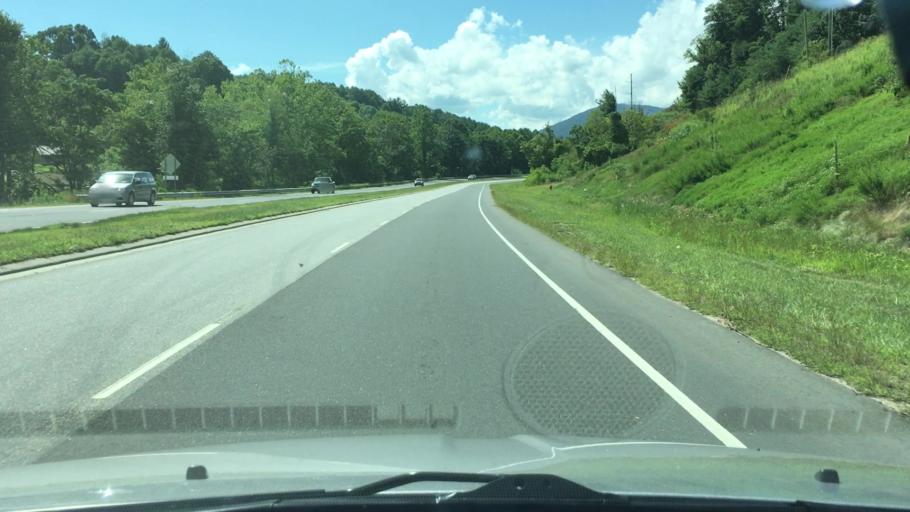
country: US
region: North Carolina
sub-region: Yancey County
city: Burnsville
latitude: 35.9112
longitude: -82.2318
